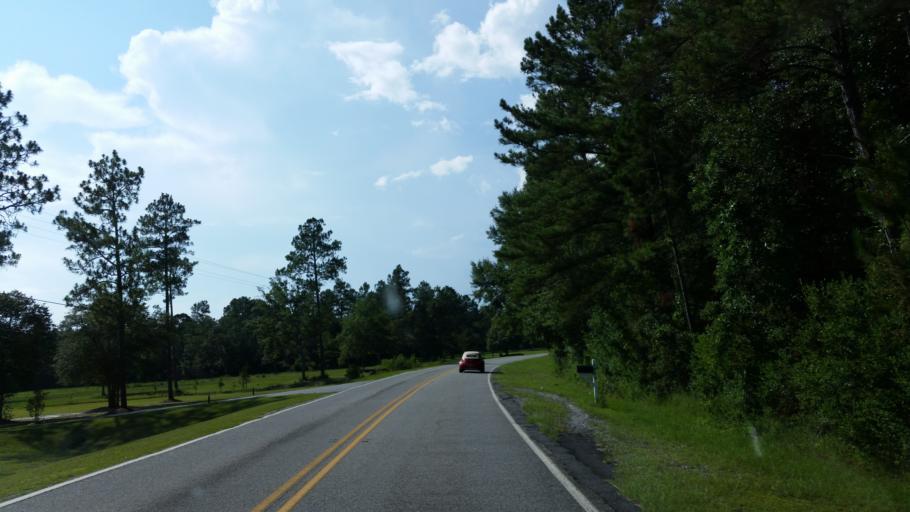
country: US
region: Georgia
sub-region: Lowndes County
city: Hahira
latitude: 30.9032
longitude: -83.3806
